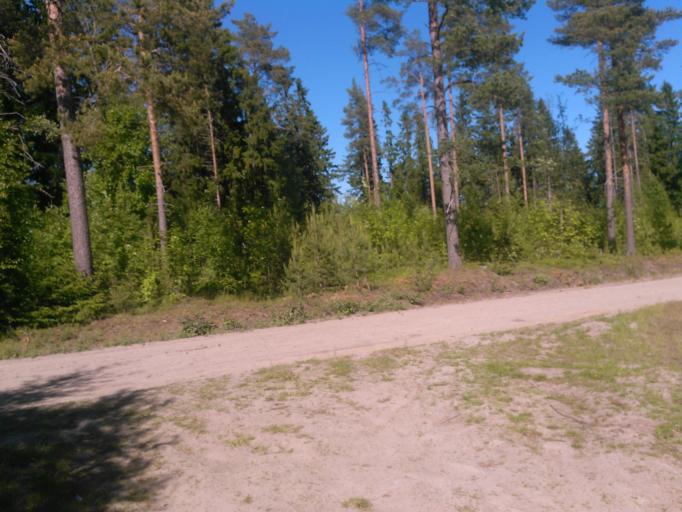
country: SE
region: Vaesterbotten
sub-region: Umea Kommun
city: Roback
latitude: 63.8262
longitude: 20.1743
